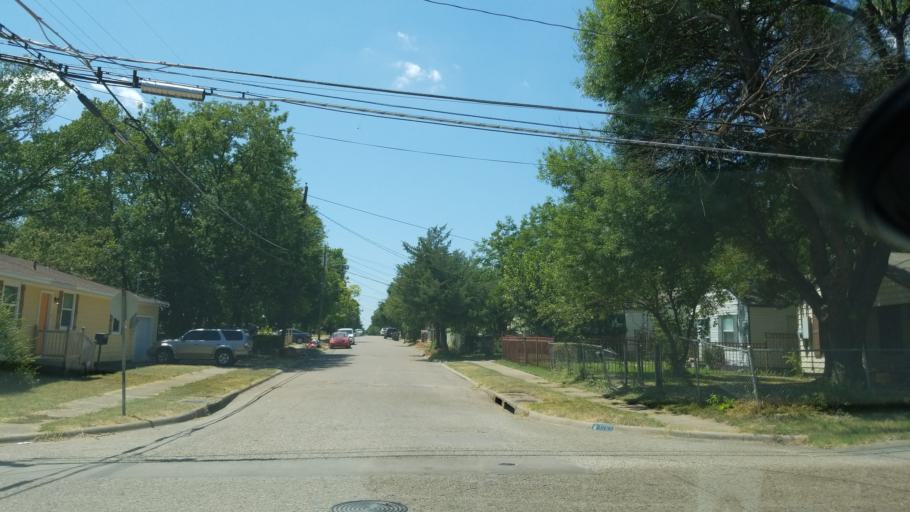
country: US
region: Texas
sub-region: Dallas County
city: Cockrell Hill
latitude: 32.7255
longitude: -96.8851
